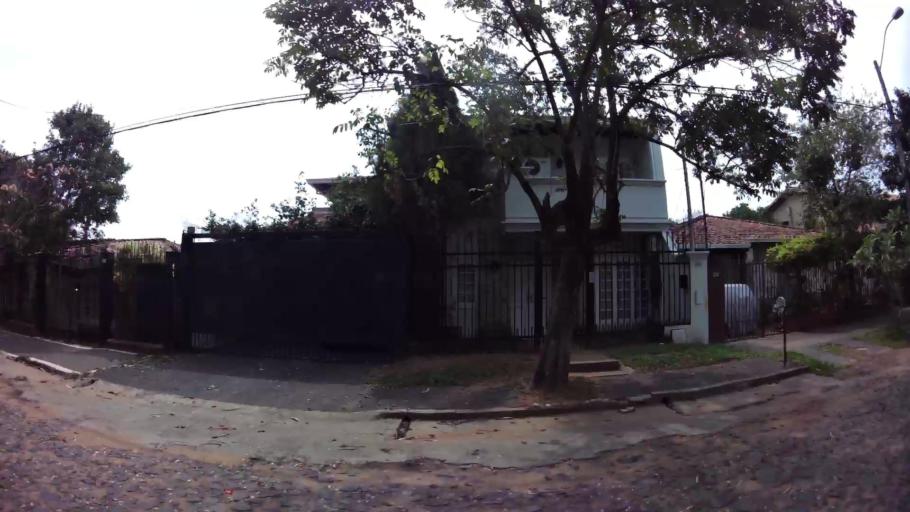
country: PY
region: Asuncion
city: Asuncion
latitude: -25.2759
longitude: -57.5737
